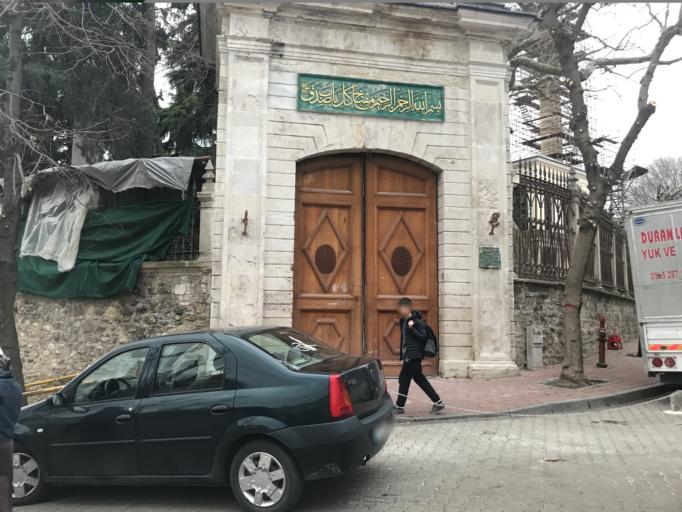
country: TR
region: Istanbul
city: Istanbul
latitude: 41.0218
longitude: 28.9423
